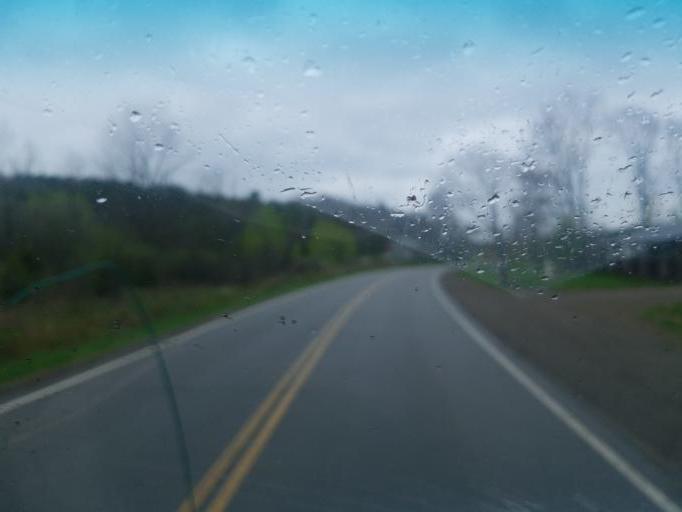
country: US
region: New York
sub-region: Allegany County
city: Belmont
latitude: 42.1713
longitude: -78.0403
